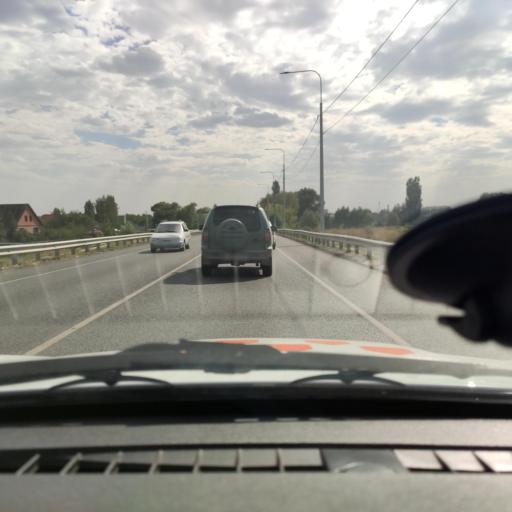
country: RU
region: Voronezj
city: Novaya Usman'
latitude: 51.6249
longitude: 39.3984
